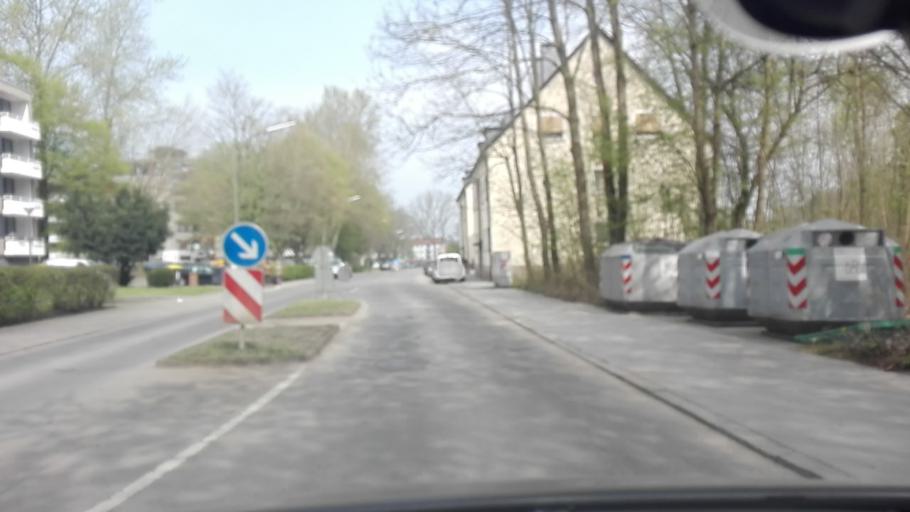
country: DE
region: North Rhine-Westphalia
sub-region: Regierungsbezirk Arnsberg
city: Dortmund
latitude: 51.4710
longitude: 7.4272
